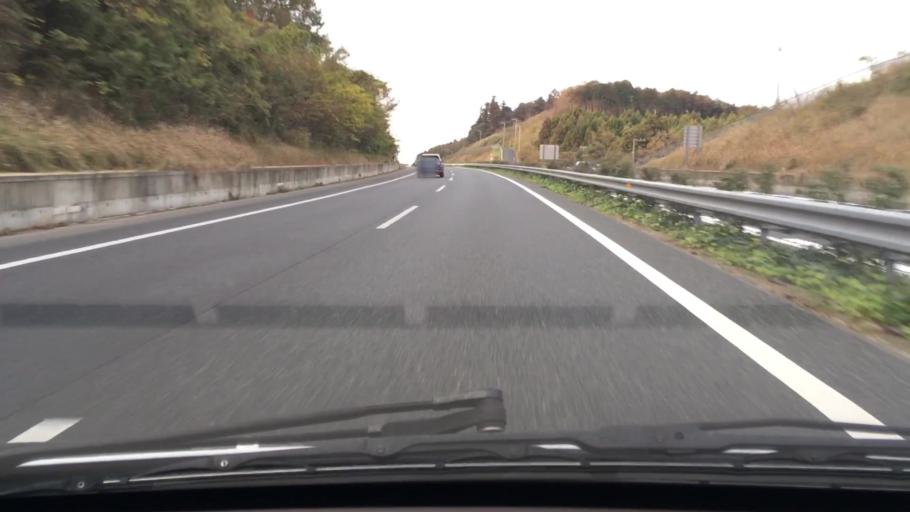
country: JP
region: Chiba
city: Kisarazu
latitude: 35.3284
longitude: 139.9463
